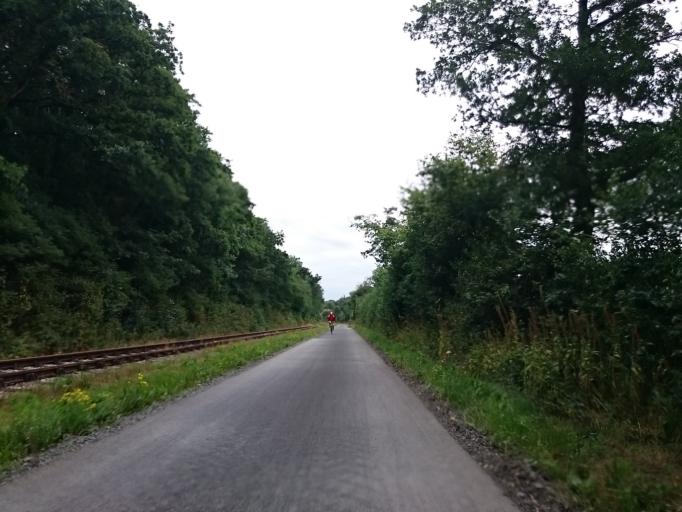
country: FR
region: Lower Normandy
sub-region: Departement du Calvados
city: Sainte-Honorine-du-Fay
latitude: 49.0375
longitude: -0.4650
